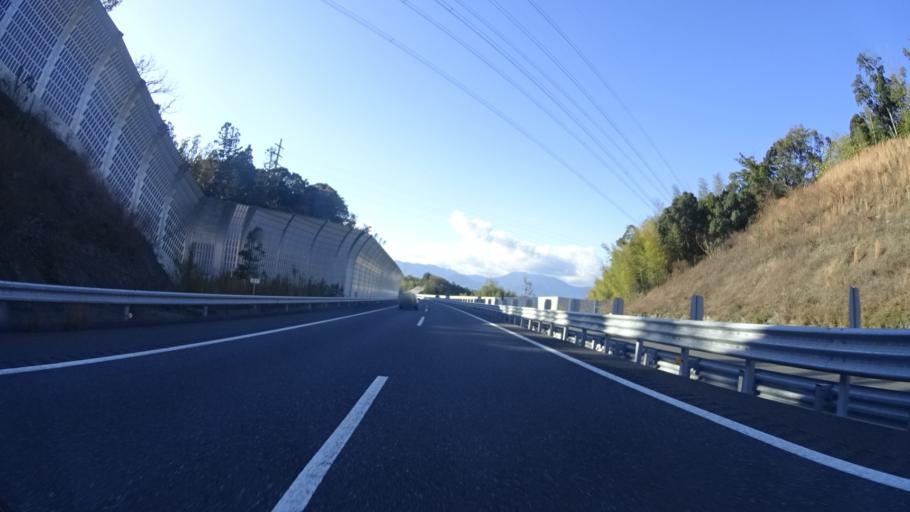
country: JP
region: Mie
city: Yokkaichi
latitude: 35.0483
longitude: 136.6106
